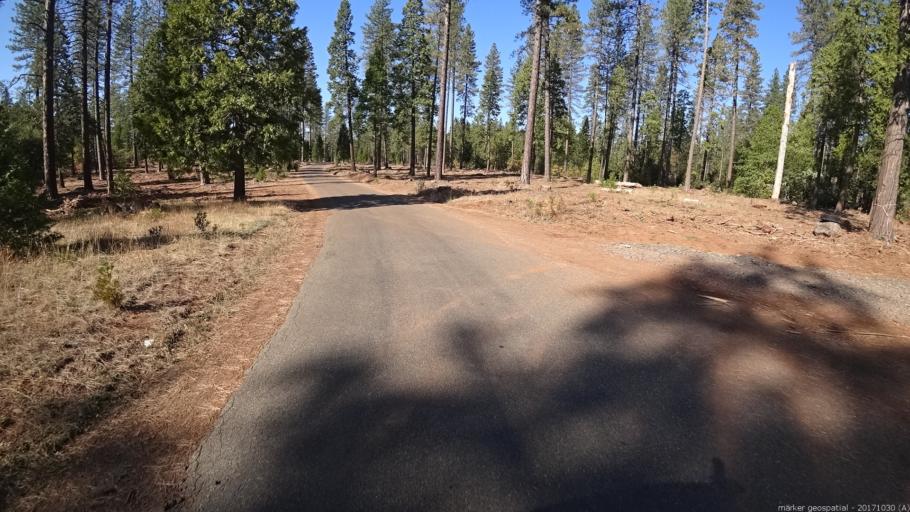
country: US
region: California
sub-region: Shasta County
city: Shingletown
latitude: 40.6077
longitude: -121.8584
